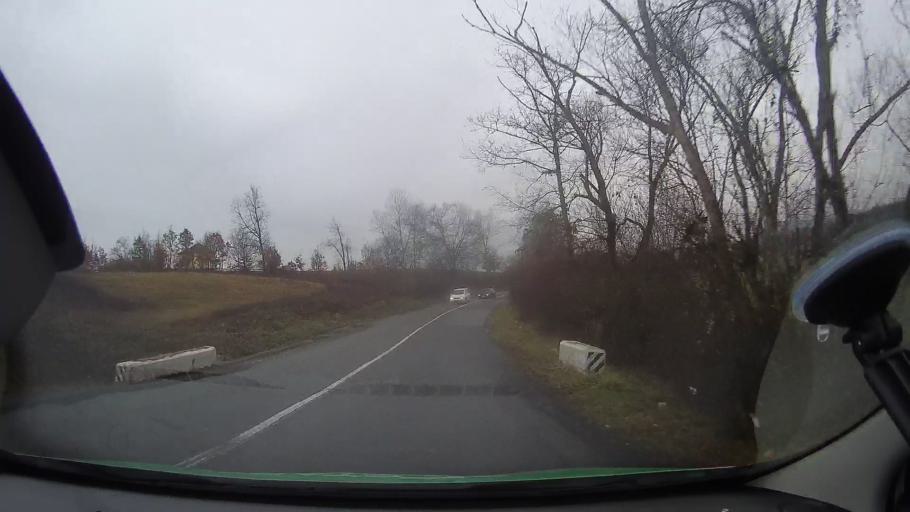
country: RO
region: Arad
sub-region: Comuna Varfurile
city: Varfurile
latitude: 46.3246
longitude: 22.4957
